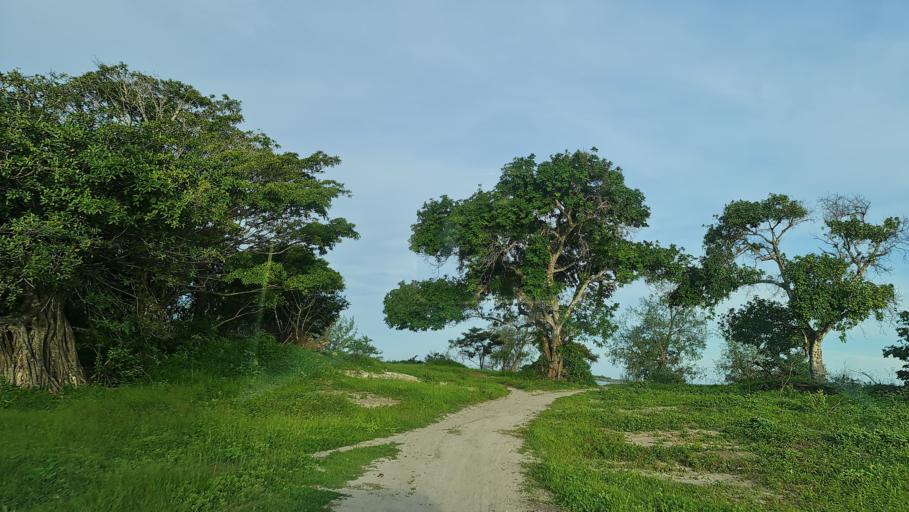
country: MZ
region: Nampula
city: Nacala
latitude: -14.7777
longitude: 40.8219
